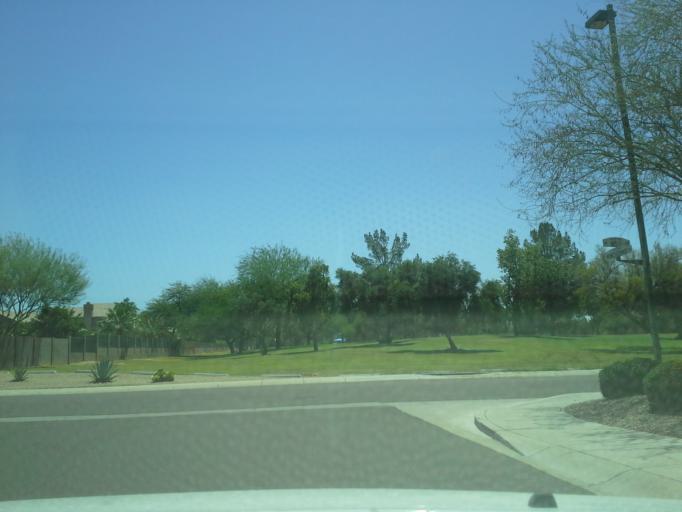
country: US
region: Arizona
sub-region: Maricopa County
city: Paradise Valley
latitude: 33.6166
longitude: -111.9413
